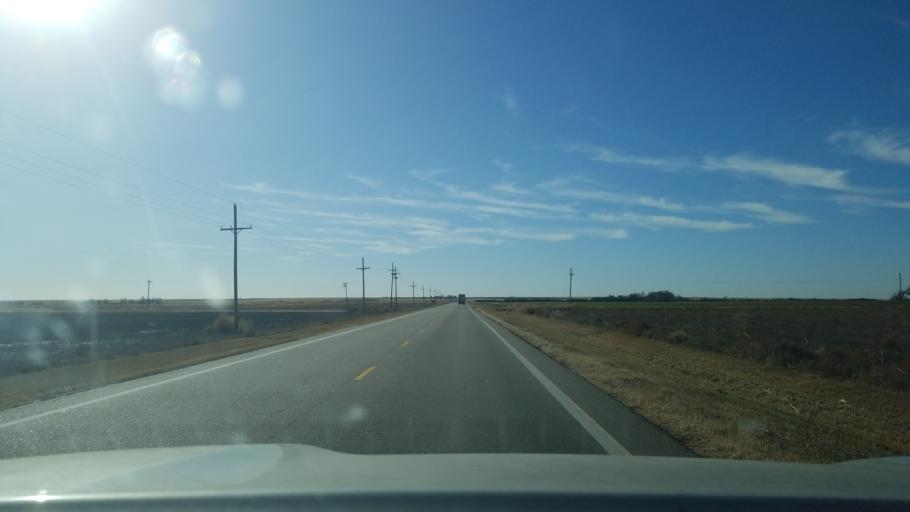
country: US
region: Kansas
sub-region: Ness County
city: Ness City
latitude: 38.4231
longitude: -99.8986
